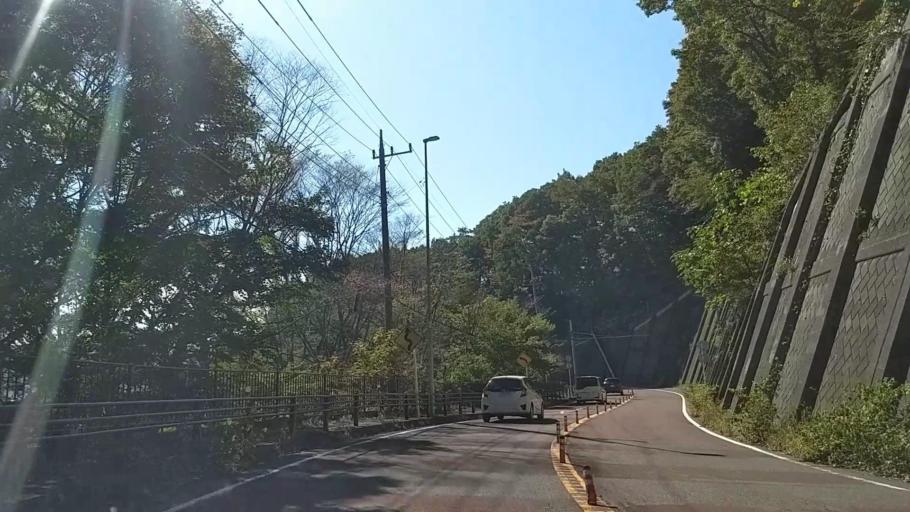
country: JP
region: Yamanashi
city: Uenohara
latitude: 35.6199
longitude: 139.2218
